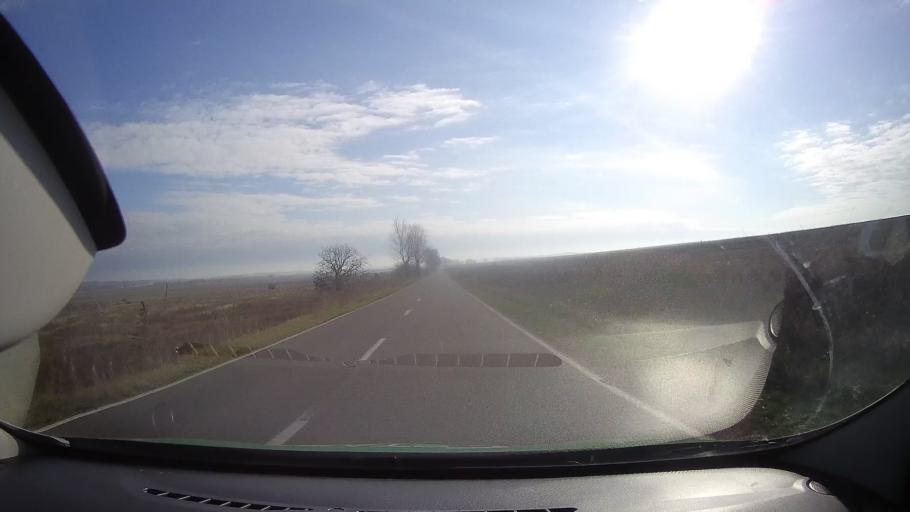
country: RO
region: Tulcea
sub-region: Comuna Mahmudia
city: Mahmudia
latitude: 45.0717
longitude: 29.0947
